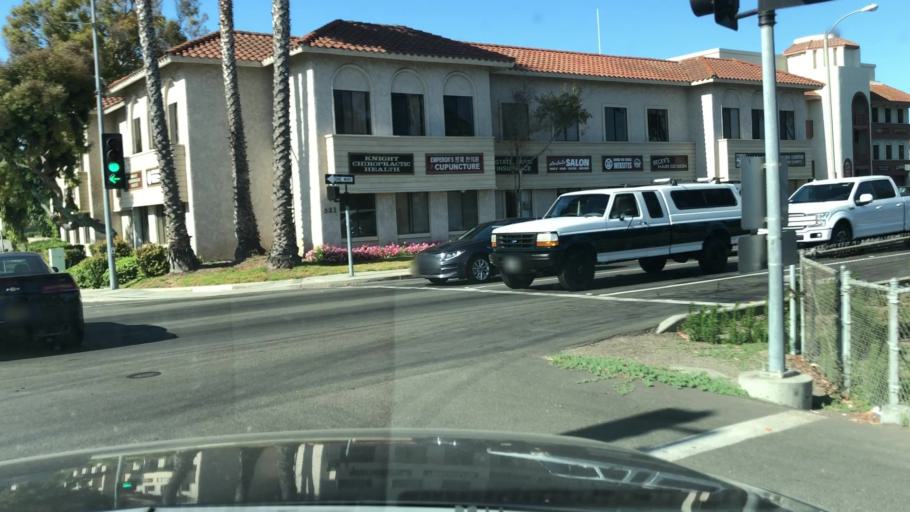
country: US
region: California
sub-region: Ventura County
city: Channel Islands Beach
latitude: 34.1759
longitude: -119.2127
